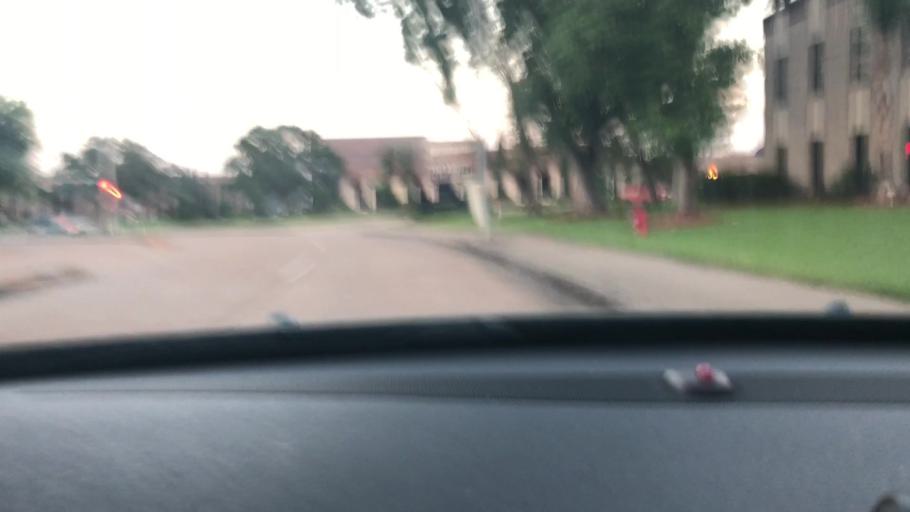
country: US
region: Texas
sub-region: Harris County
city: Webster
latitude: 29.5516
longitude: -95.1169
